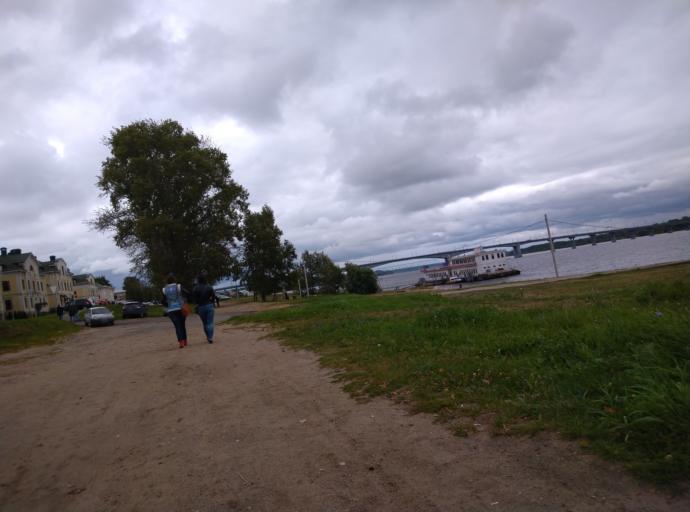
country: RU
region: Kostroma
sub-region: Kostromskoy Rayon
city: Kostroma
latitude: 57.7601
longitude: 40.9328
